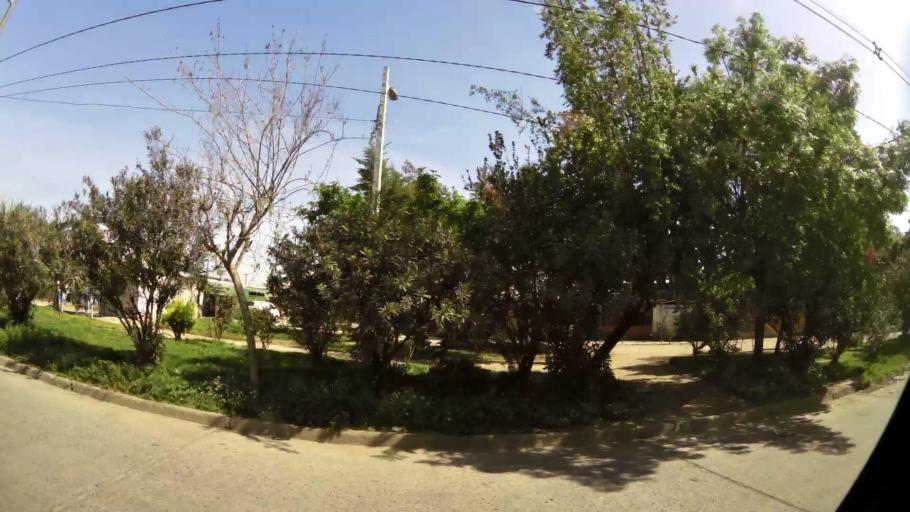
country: CL
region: Santiago Metropolitan
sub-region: Provincia de Maipo
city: San Bernardo
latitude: -33.5234
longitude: -70.7003
